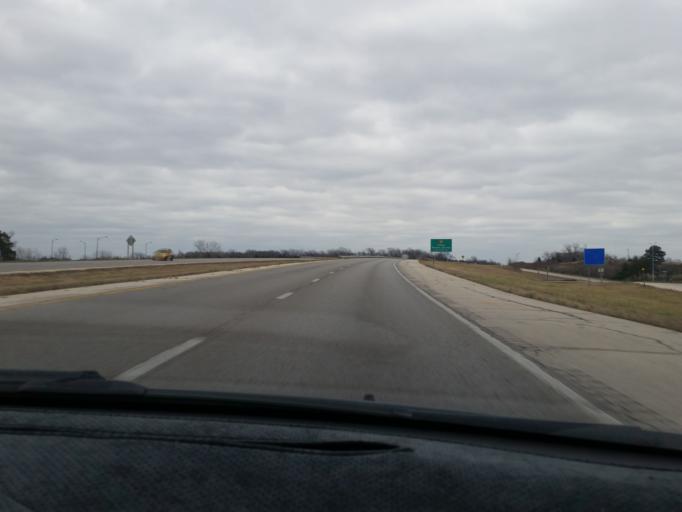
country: US
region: Kansas
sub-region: Johnson County
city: De Soto
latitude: 38.9478
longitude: -94.8884
